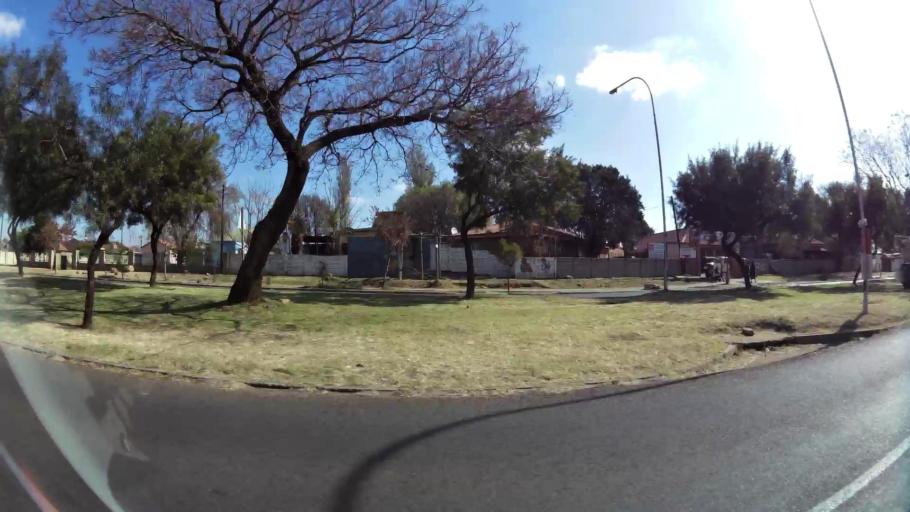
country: ZA
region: Gauteng
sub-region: City of Johannesburg Metropolitan Municipality
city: Soweto
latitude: -26.2594
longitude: 27.8855
